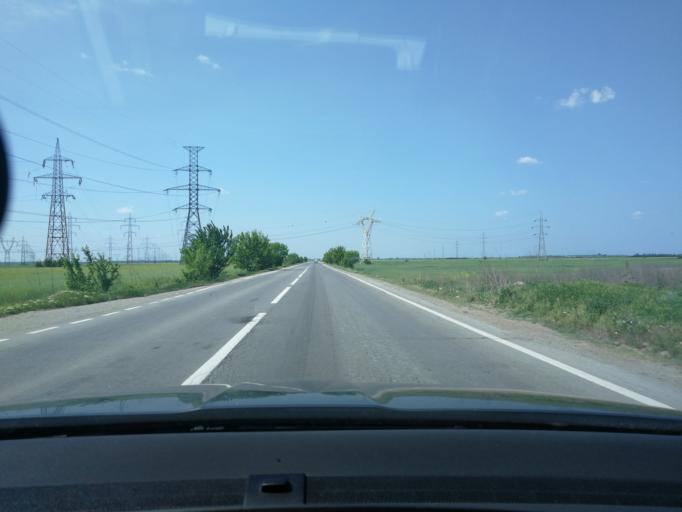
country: RO
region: Prahova
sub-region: Comuna Brazi
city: Negoiesti
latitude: 44.8970
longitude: 25.9691
